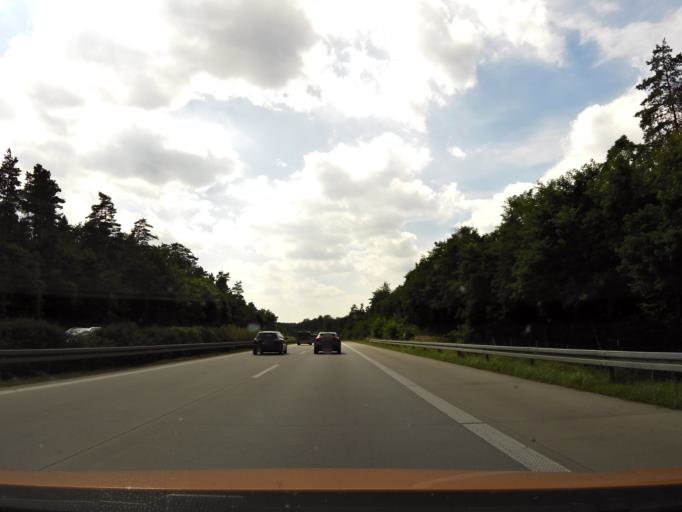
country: DE
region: Brandenburg
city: Rudnitz
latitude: 52.7680
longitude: 13.5557
